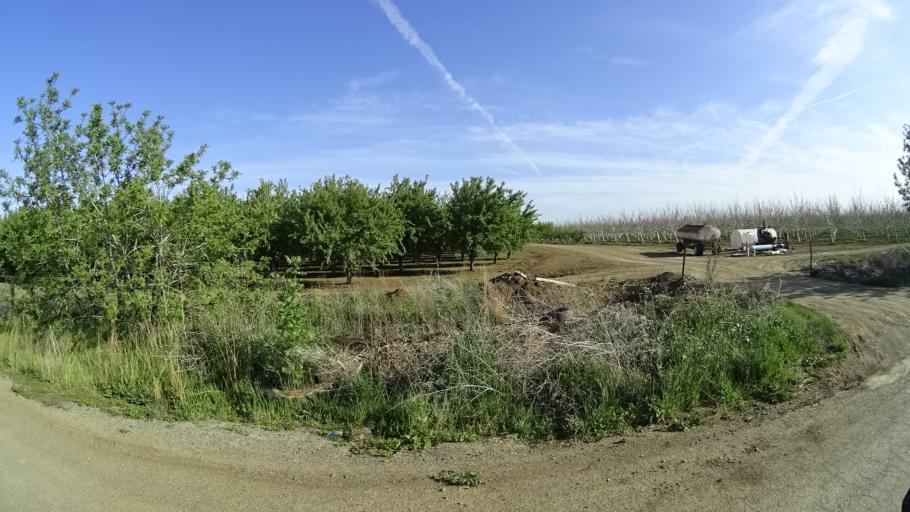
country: US
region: California
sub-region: Glenn County
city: Willows
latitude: 39.5534
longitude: -122.2374
